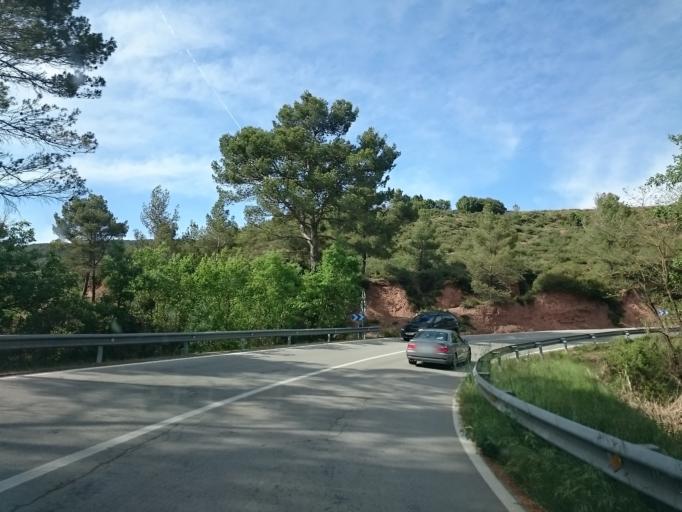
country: ES
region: Catalonia
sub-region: Provincia de Barcelona
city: Jorba
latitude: 41.5795
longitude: 1.5407
